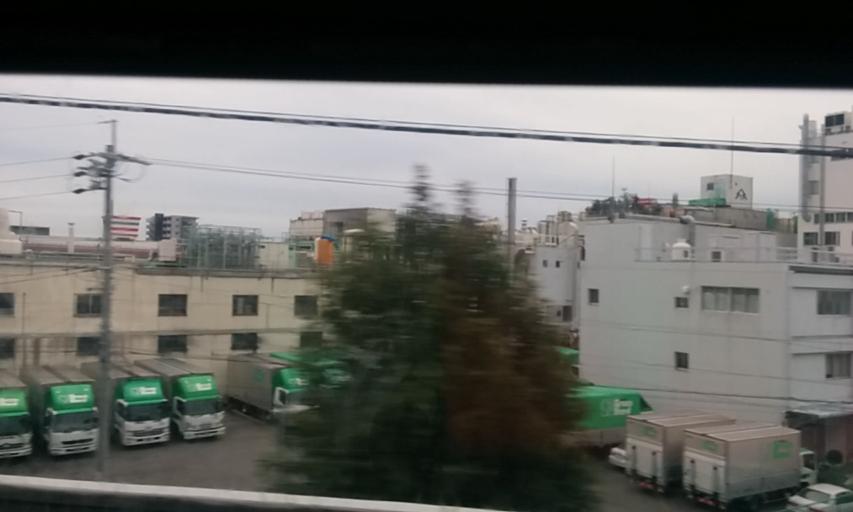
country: JP
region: Aichi
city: Nagoya-shi
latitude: 35.1457
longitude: 136.9081
